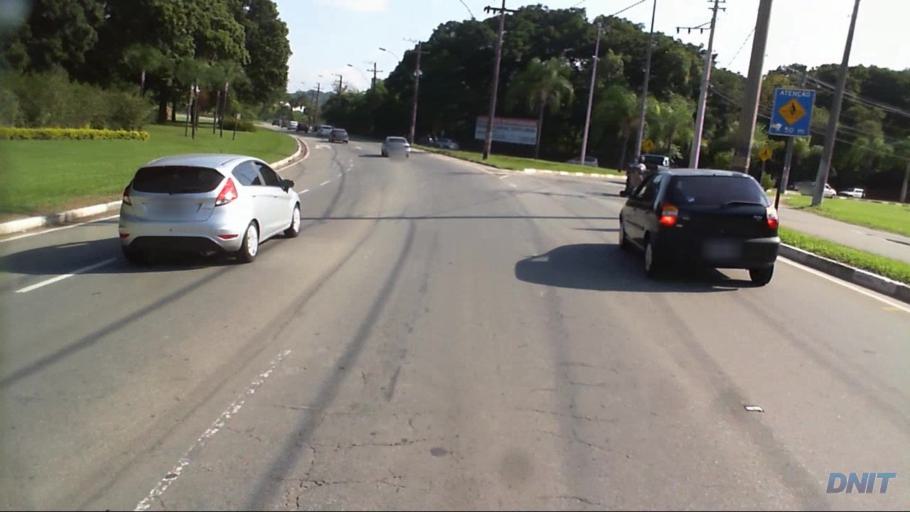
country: BR
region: Minas Gerais
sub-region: Ipatinga
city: Ipatinga
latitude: -19.4842
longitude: -42.5545
